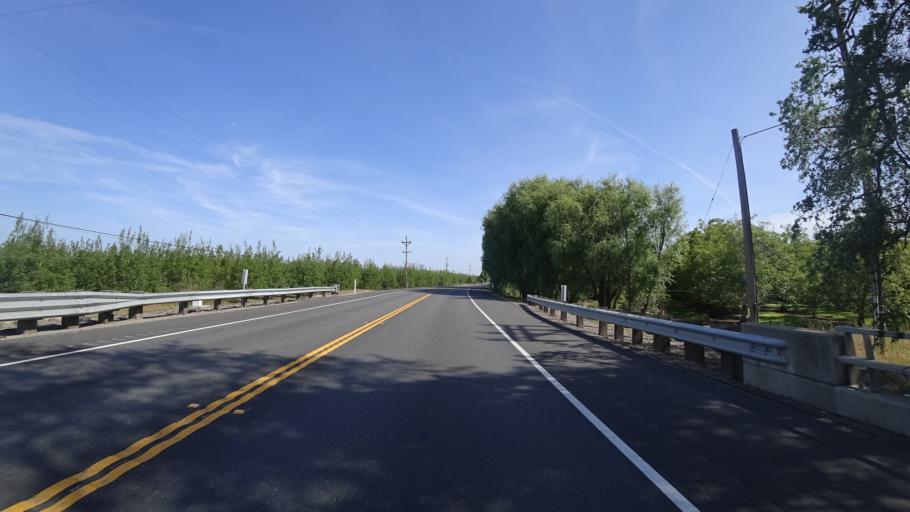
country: US
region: California
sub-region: Glenn County
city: Hamilton City
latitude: 39.8787
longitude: -121.9709
